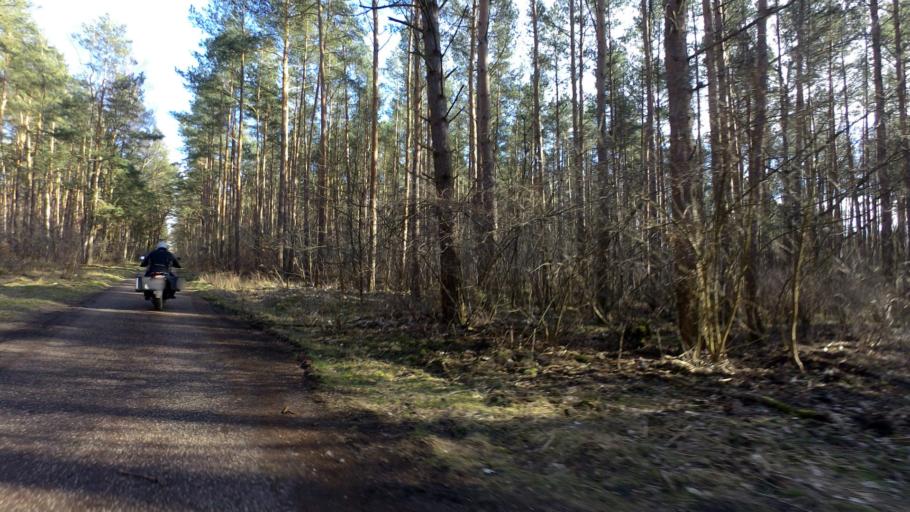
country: DE
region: Brandenburg
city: Oranienburg
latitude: 52.7550
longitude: 13.2793
